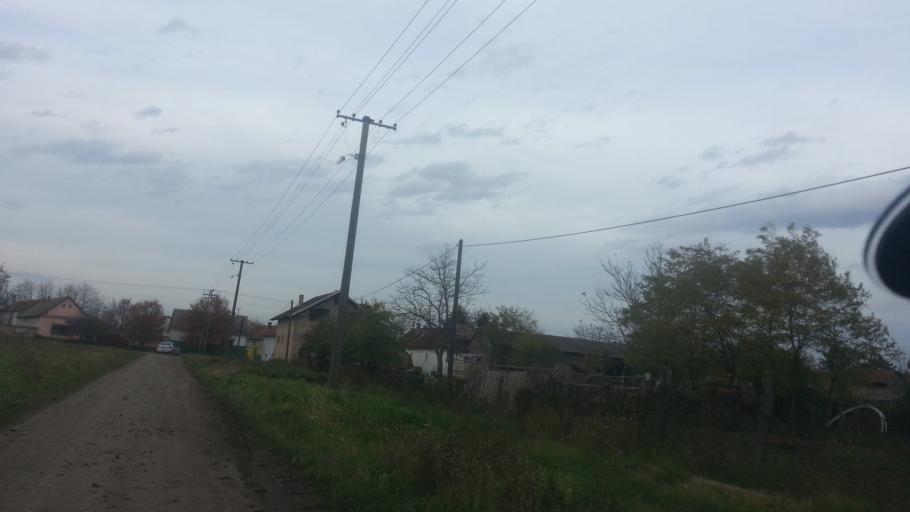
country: RS
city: Putinci
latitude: 44.9653
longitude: 19.9677
